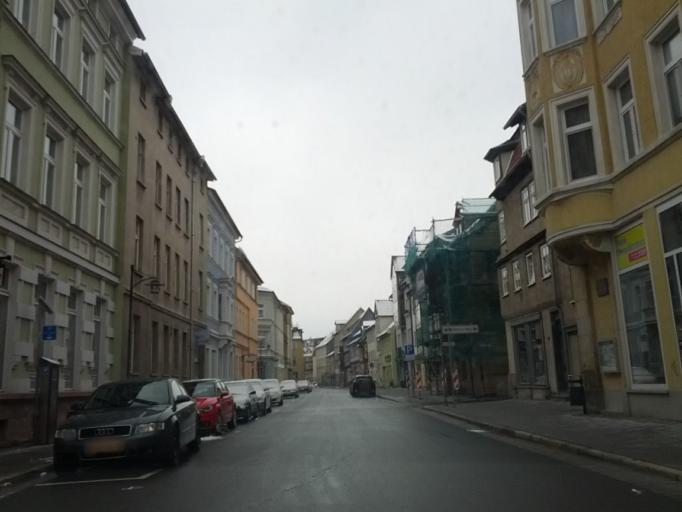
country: DE
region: Thuringia
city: Meiningen
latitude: 50.5690
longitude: 10.4140
